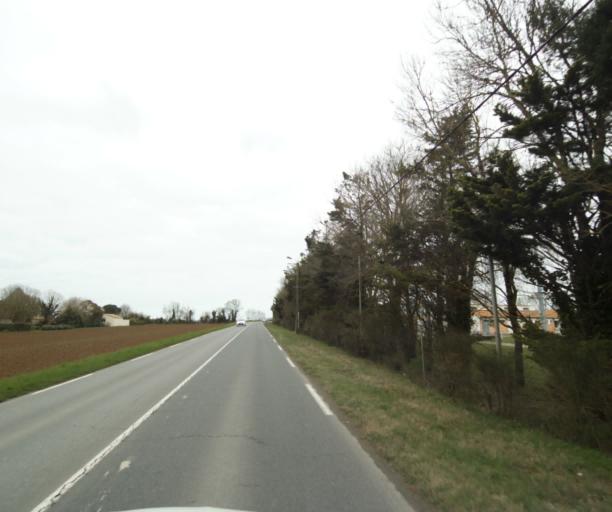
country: FR
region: Poitou-Charentes
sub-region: Departement de la Charente-Maritime
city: Lagord
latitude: 46.1953
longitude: -1.1547
